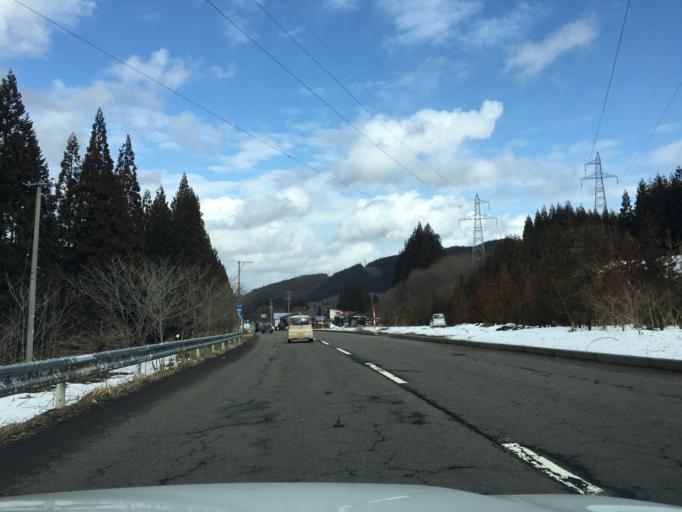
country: JP
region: Akita
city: Takanosu
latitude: 40.0053
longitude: 140.2785
